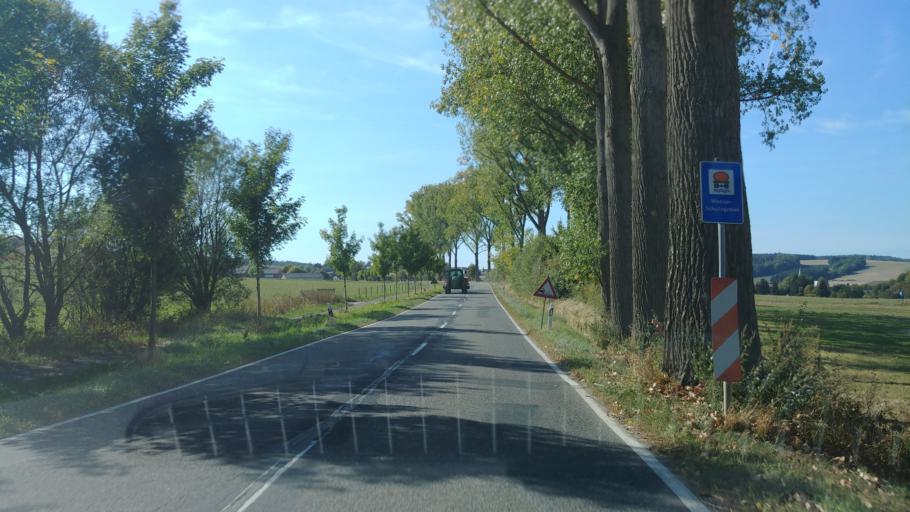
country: DE
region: Hesse
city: Burg Hohenstein
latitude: 50.1917
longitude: 8.1111
